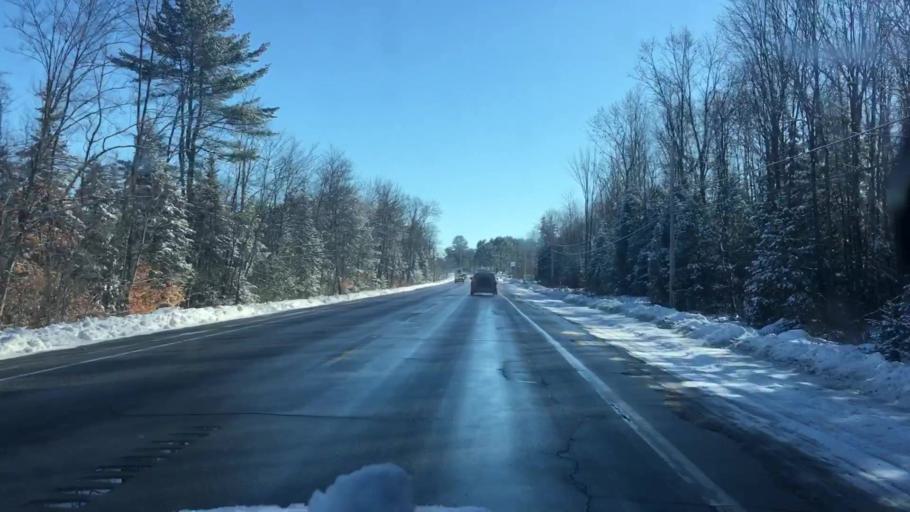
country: US
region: Maine
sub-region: Cumberland County
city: Bridgton
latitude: 44.0280
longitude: -70.6935
